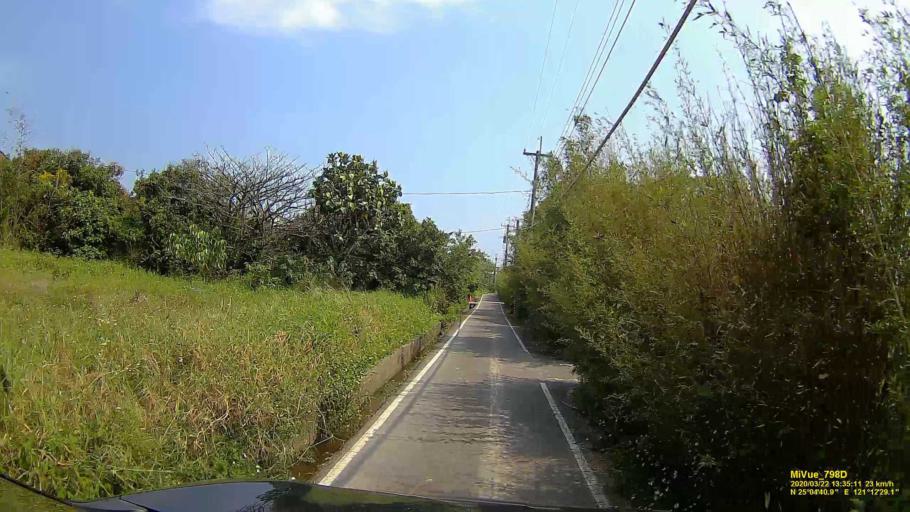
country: TW
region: Taiwan
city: Taoyuan City
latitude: 25.0779
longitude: 121.2082
